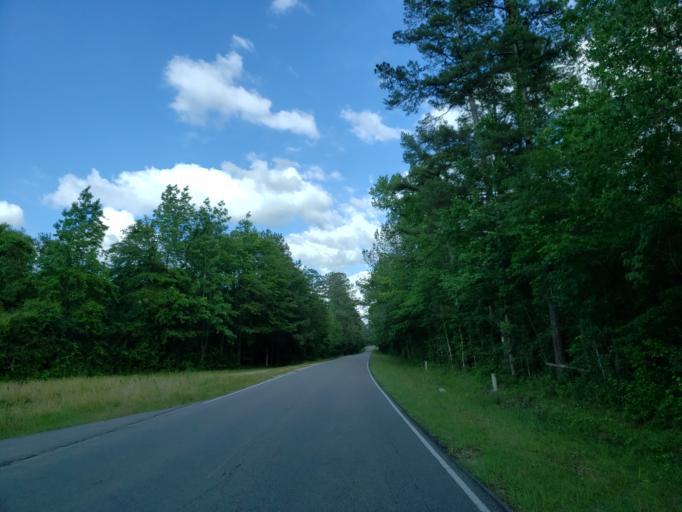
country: US
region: Mississippi
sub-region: Forrest County
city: Petal
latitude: 31.3110
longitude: -89.2281
